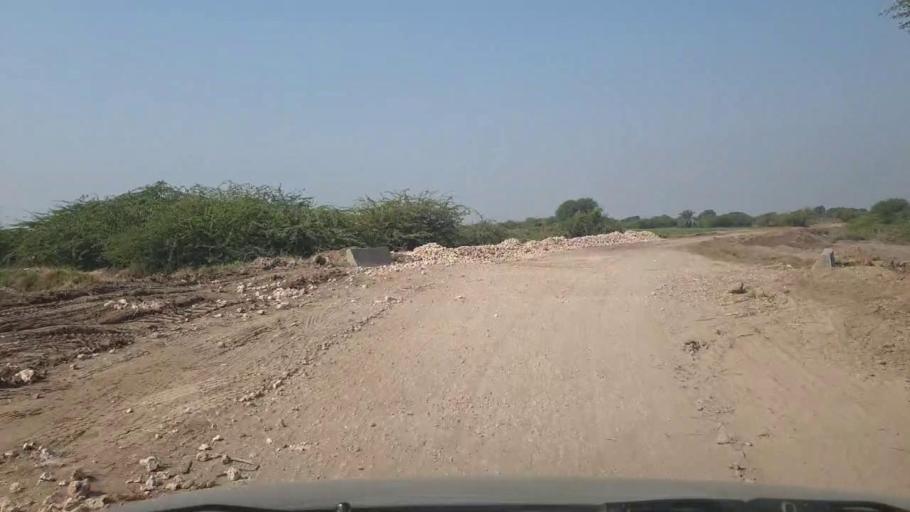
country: PK
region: Sindh
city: Mirwah Gorchani
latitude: 25.2467
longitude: 69.1080
